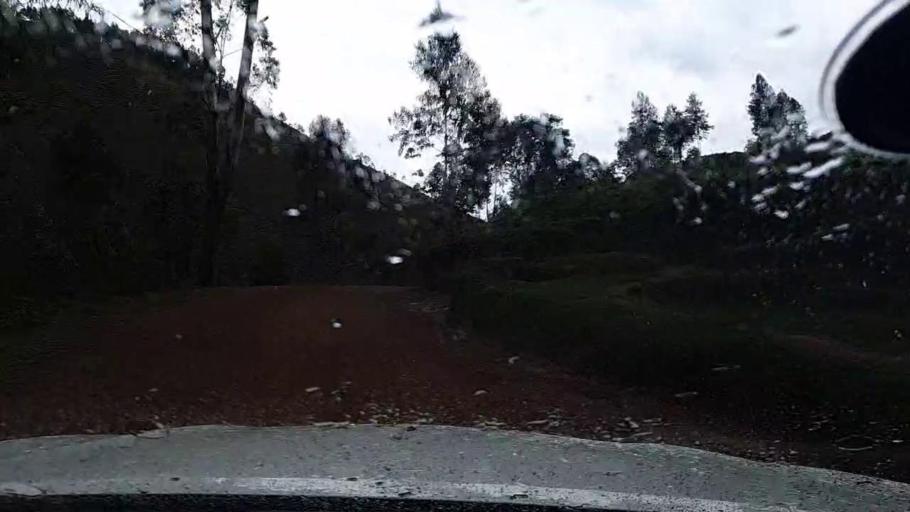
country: RW
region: Western Province
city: Kibuye
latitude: -2.1600
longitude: 29.4353
